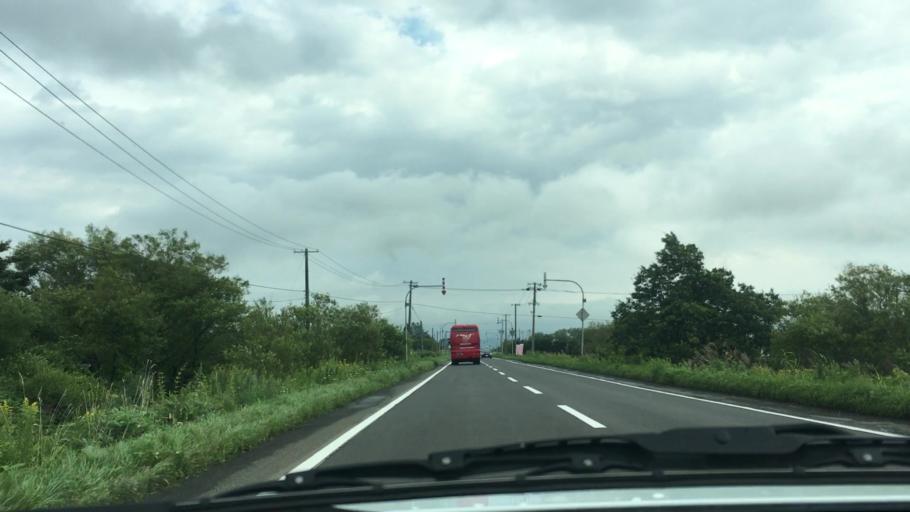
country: JP
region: Hokkaido
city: Chitose
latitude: 42.9438
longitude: 141.7635
